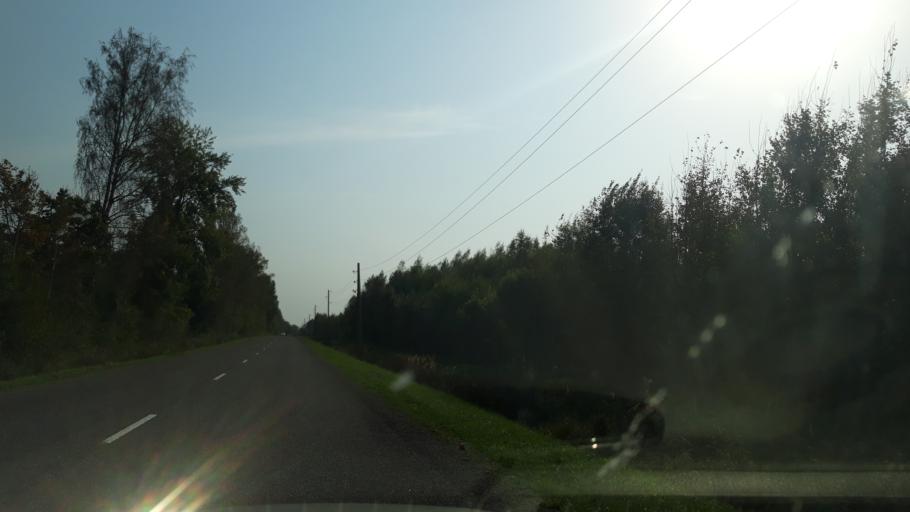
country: LV
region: Burtnieki
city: Matisi
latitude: 57.6344
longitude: 25.2577
